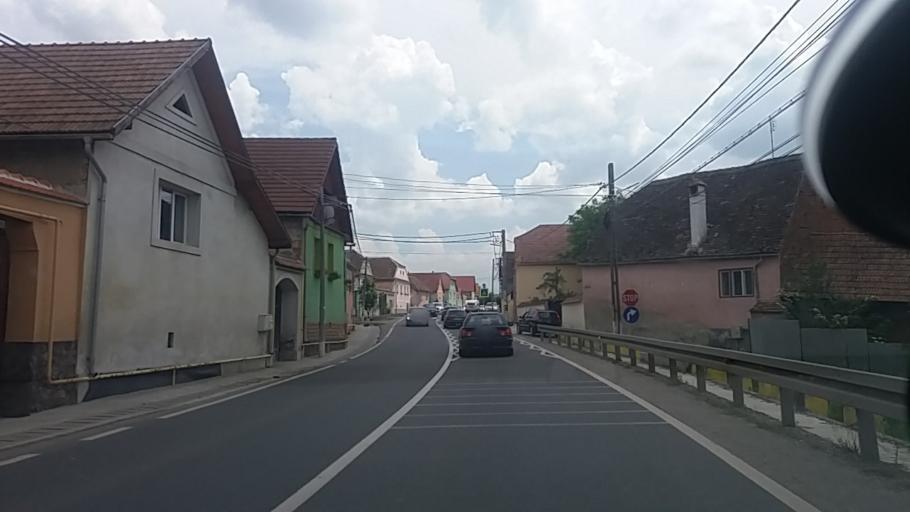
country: RO
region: Sibiu
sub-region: Comuna Slimnic
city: Slimnic
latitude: 45.9592
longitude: 24.1653
